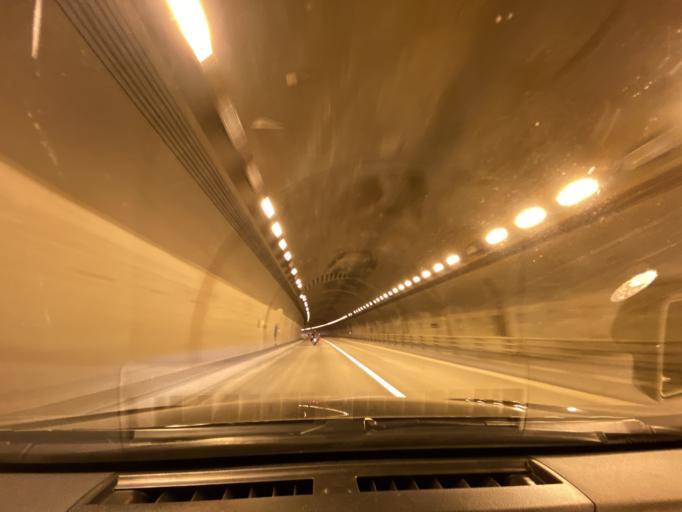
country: JP
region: Hokkaido
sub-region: Asahikawa-shi
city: Asahikawa
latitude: 43.8470
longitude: 142.4530
